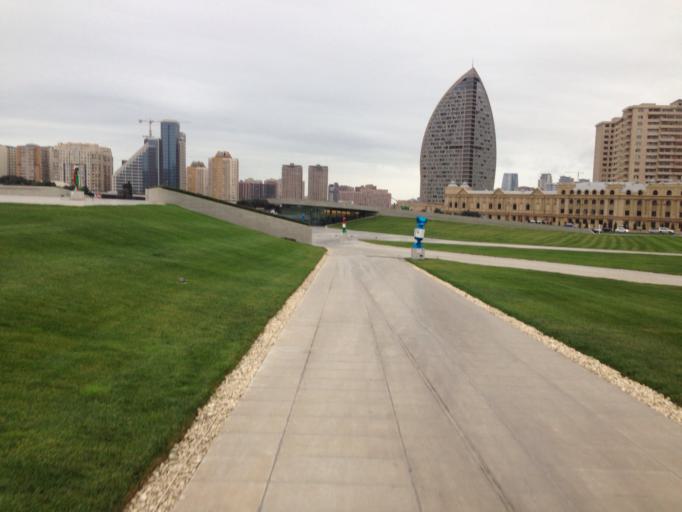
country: AZ
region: Baki
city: Baku
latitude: 40.3947
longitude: 49.8652
